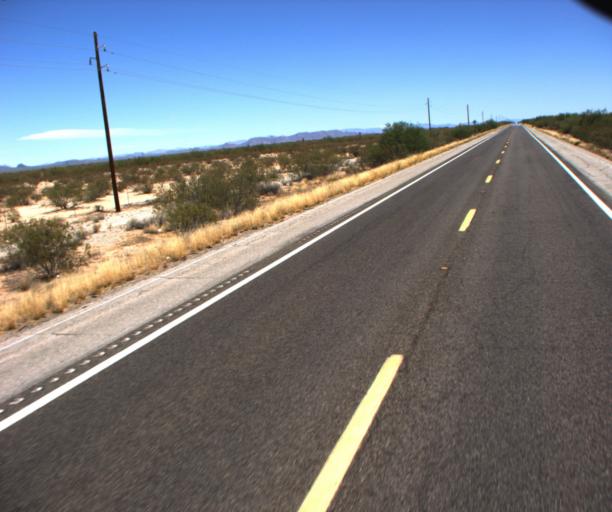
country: US
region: Arizona
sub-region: La Paz County
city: Salome
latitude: 33.8874
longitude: -113.3437
